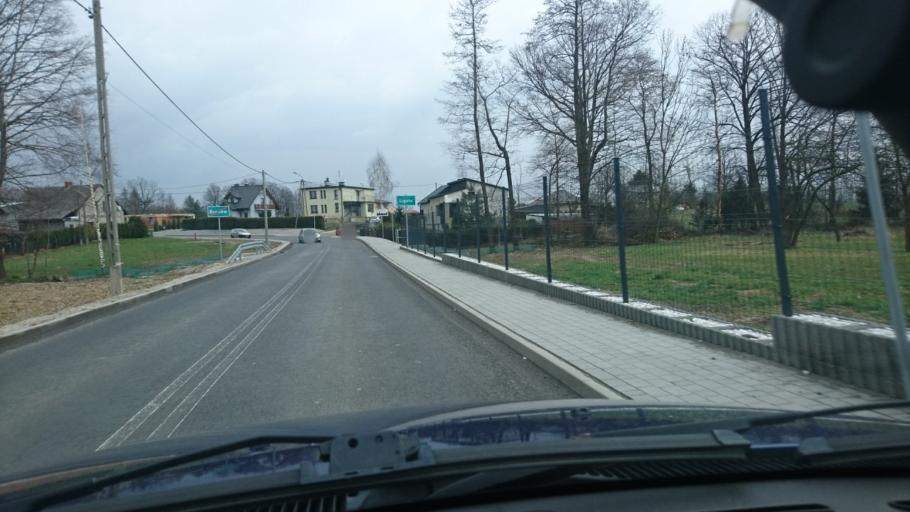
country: PL
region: Silesian Voivodeship
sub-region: Powiat bielski
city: Bronow
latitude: 49.8783
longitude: 18.9246
